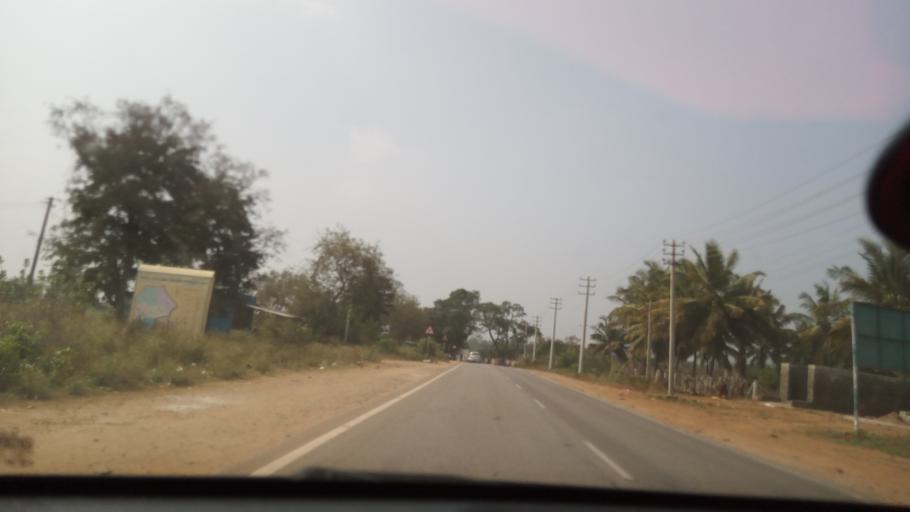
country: IN
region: Karnataka
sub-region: Chamrajnagar
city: Chamrajnagar
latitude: 11.9926
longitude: 76.8616
